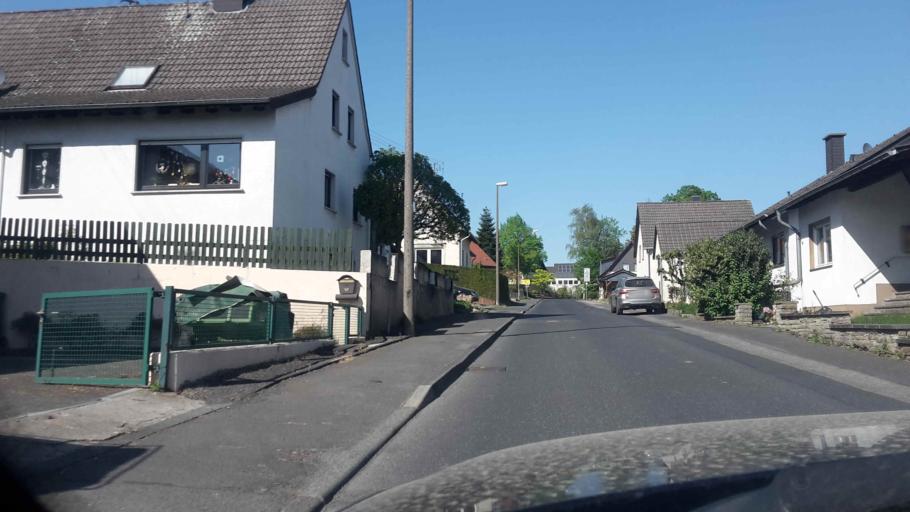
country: DE
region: Rheinland-Pfalz
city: Windhagen
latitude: 50.6852
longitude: 7.3347
